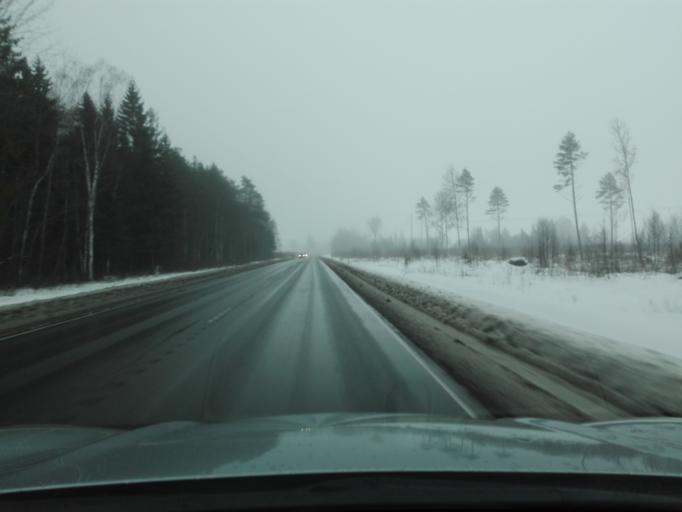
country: EE
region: Raplamaa
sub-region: Kohila vald
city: Kohila
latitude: 59.2365
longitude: 24.7648
